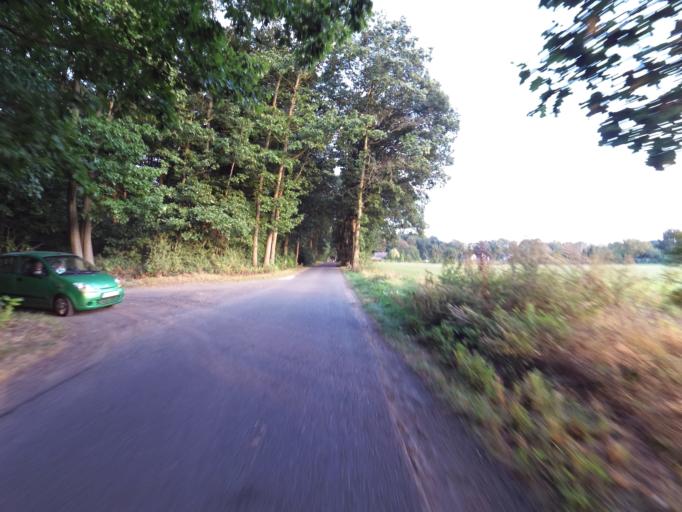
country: DE
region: North Rhine-Westphalia
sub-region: Regierungsbezirk Dusseldorf
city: Emmerich
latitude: 51.8601
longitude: 6.1927
